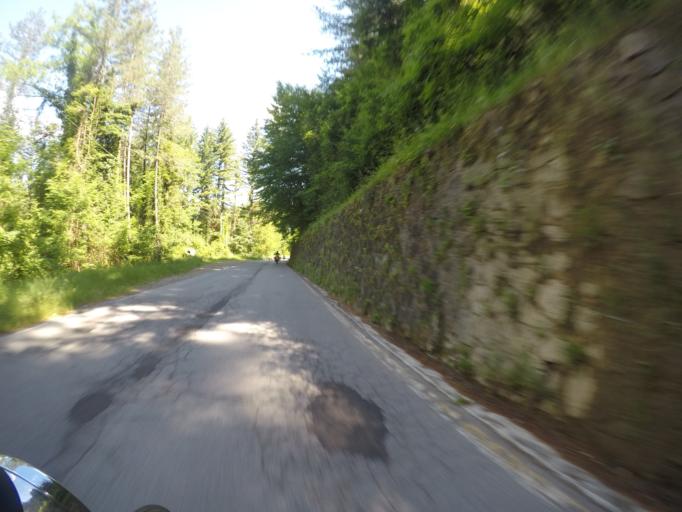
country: IT
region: Tuscany
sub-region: Provincia di Lucca
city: Camporgiano
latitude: 44.1387
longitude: 10.3470
